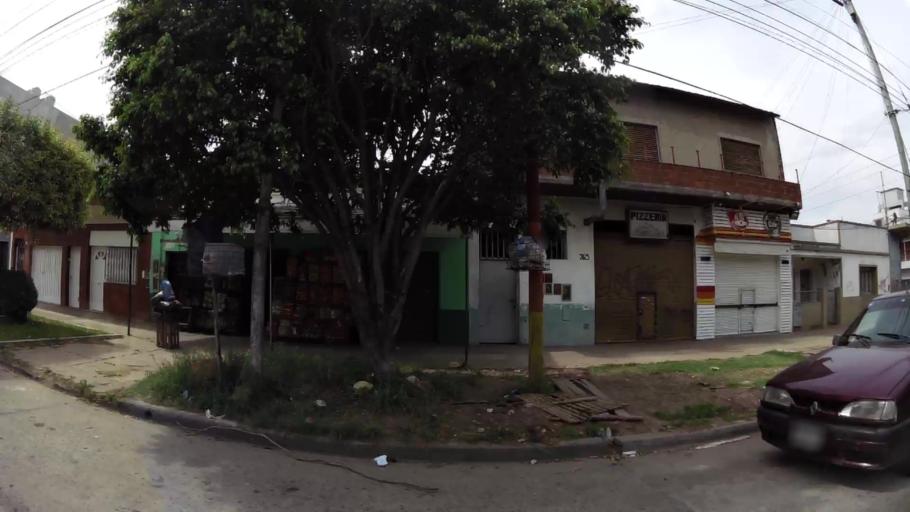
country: AR
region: Buenos Aires F.D.
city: Villa Lugano
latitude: -34.6905
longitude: -58.4985
